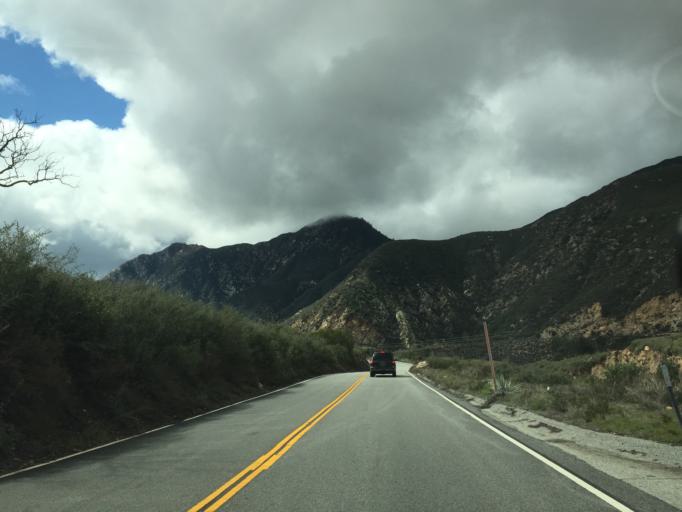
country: US
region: California
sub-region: Los Angeles County
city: Glendora
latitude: 34.2921
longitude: -117.8344
